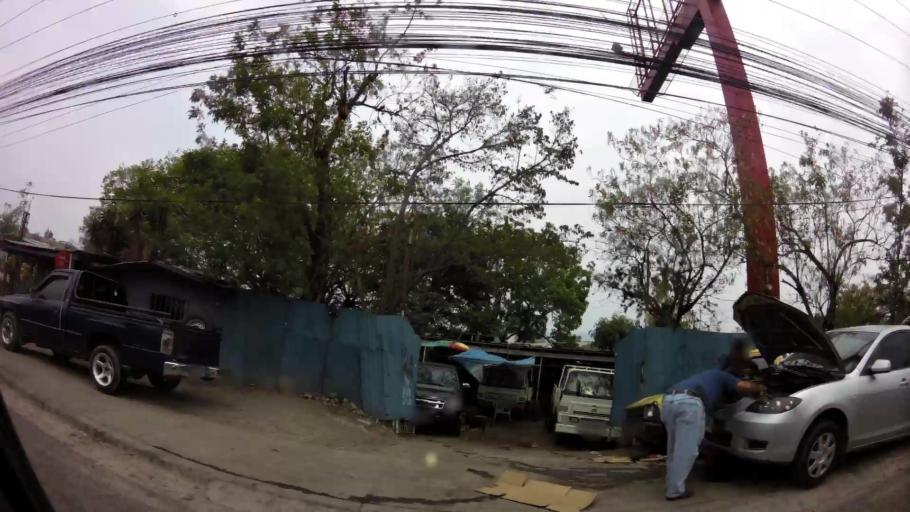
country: HN
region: Francisco Morazan
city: Tegucigalpa
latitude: 14.0738
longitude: -87.2115
